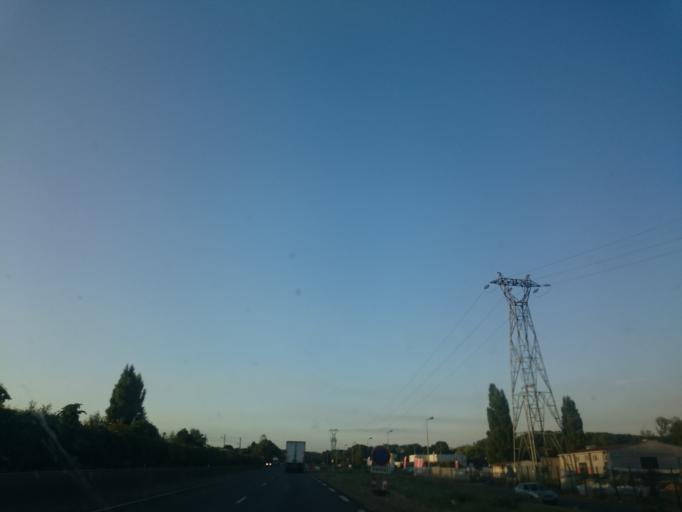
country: FR
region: Ile-de-France
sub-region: Departement de l'Essonne
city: Etrechy
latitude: 48.4892
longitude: 2.1969
